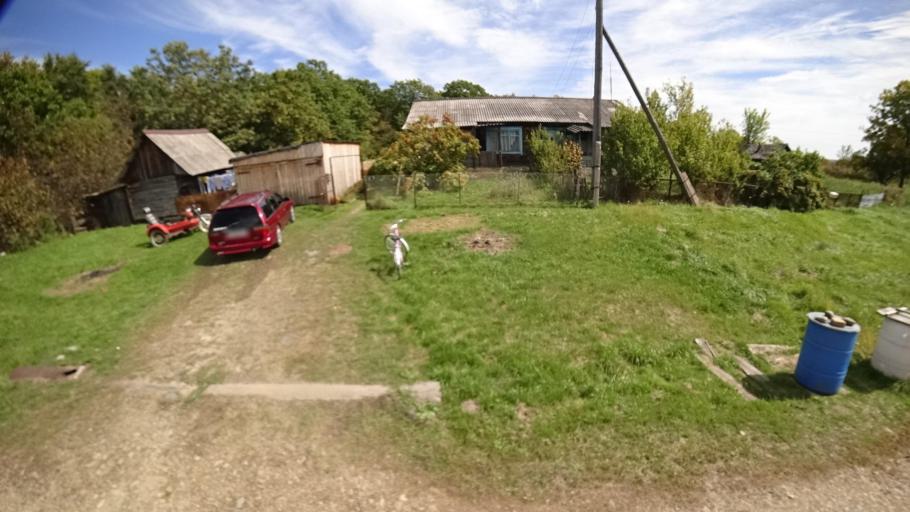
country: RU
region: Primorskiy
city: Yakovlevka
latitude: 44.6488
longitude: 133.5879
